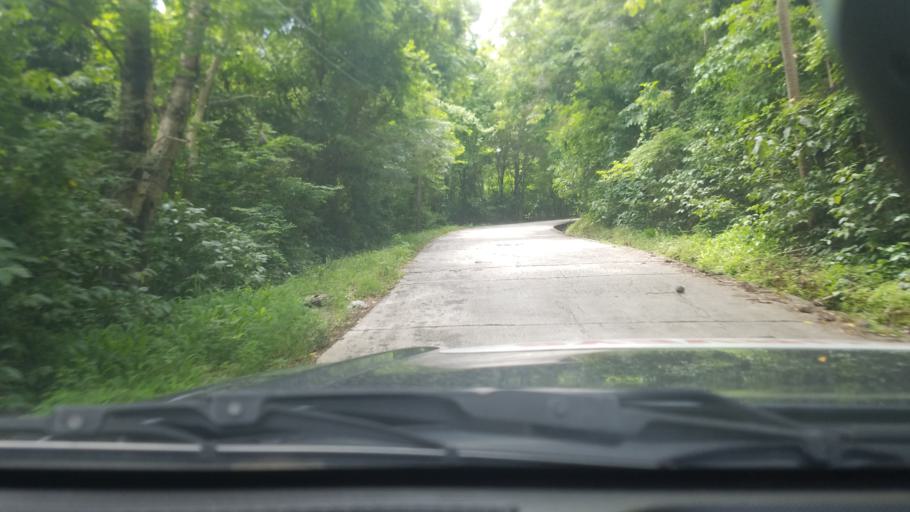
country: LC
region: Soufriere
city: Soufriere
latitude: 13.8365
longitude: -61.0602
